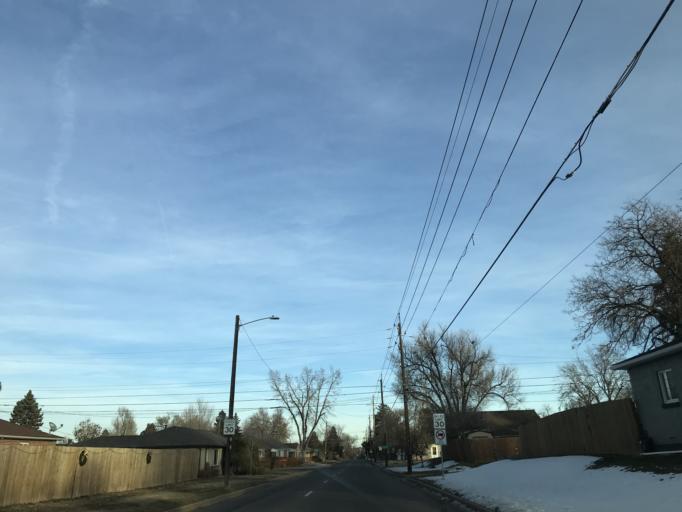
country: US
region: Colorado
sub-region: Arapahoe County
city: Glendale
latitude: 39.7387
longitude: -104.8987
